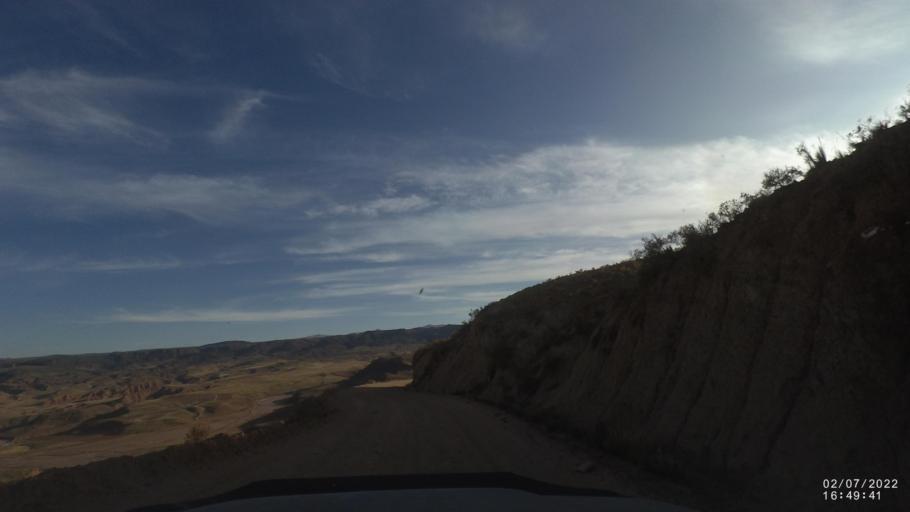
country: BO
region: Cochabamba
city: Irpa Irpa
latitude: -17.9745
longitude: -66.5277
